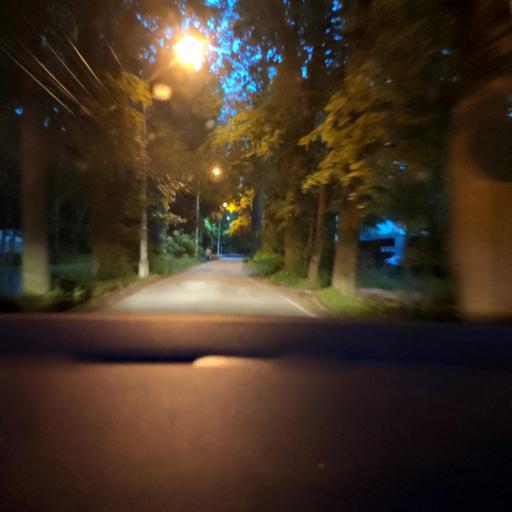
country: RU
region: Moskovskaya
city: Saltykovka
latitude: 55.7502
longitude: 37.9214
